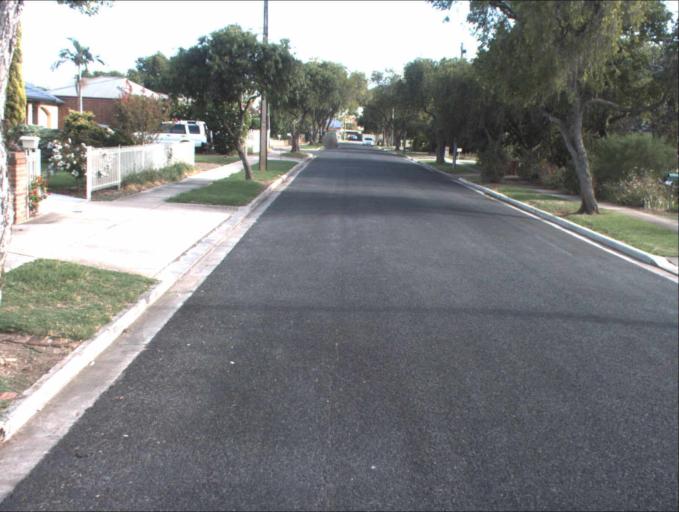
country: AU
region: South Australia
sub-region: Port Adelaide Enfield
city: Klemzig
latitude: -34.8743
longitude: 138.6233
